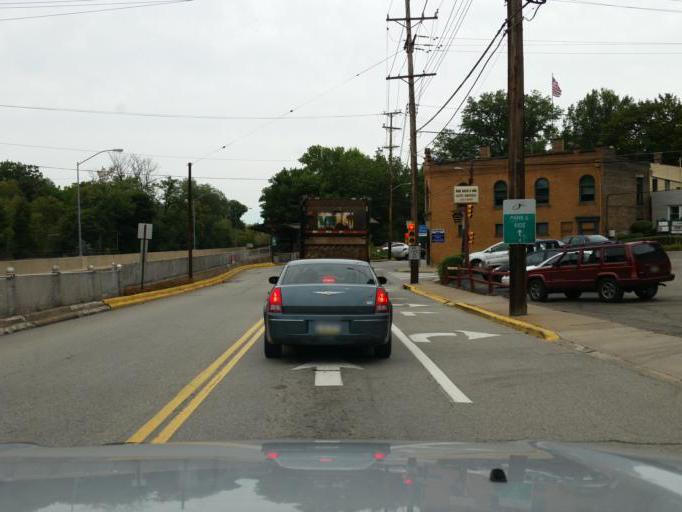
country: US
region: Pennsylvania
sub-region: Allegheny County
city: Edgewood
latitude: 40.4325
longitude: -79.8847
